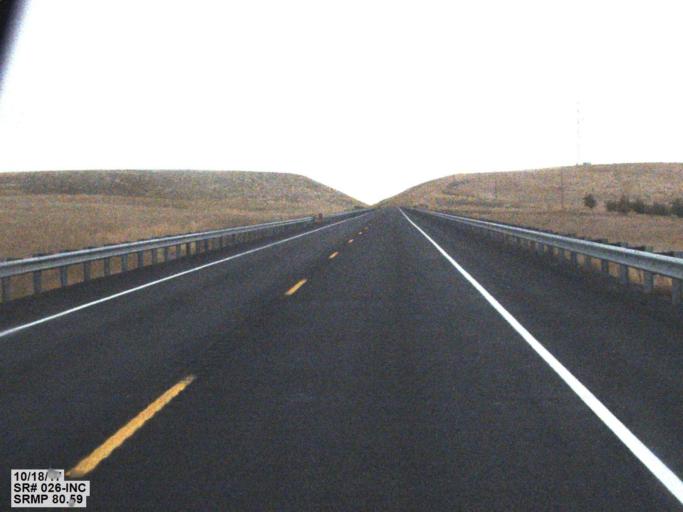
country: US
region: Washington
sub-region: Adams County
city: Ritzville
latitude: 46.7712
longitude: -118.3536
